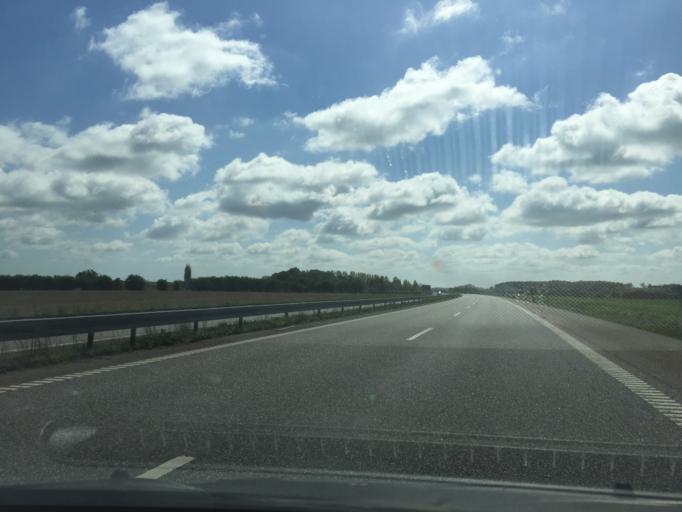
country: DK
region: Zealand
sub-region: Guldborgsund Kommune
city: Sundby
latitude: 54.8550
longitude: 11.8383
